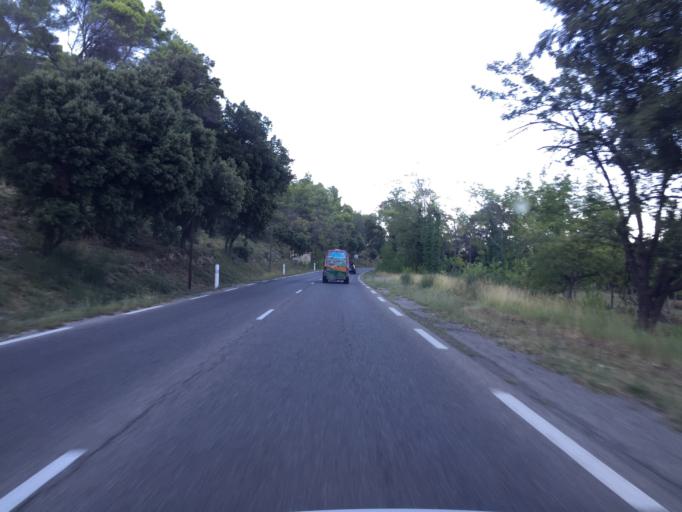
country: FR
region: Provence-Alpes-Cote d'Azur
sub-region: Departement des Alpes-de-Haute-Provence
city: Peyruis
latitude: 43.9900
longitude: 5.9136
